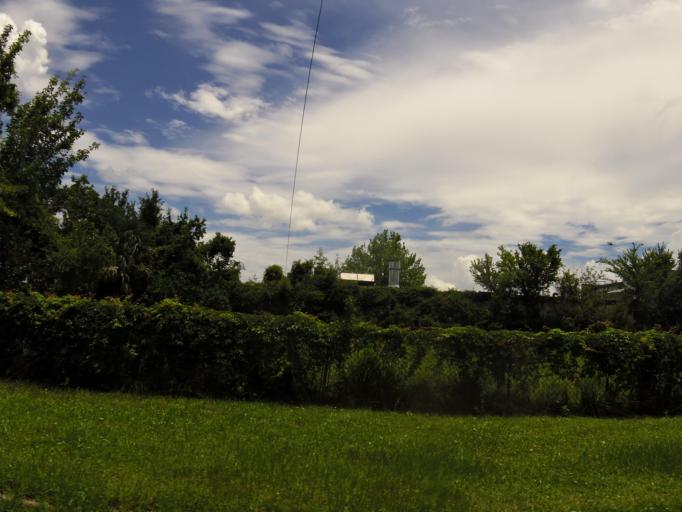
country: US
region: Florida
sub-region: Duval County
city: Jacksonville
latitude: 30.3472
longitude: -81.6475
